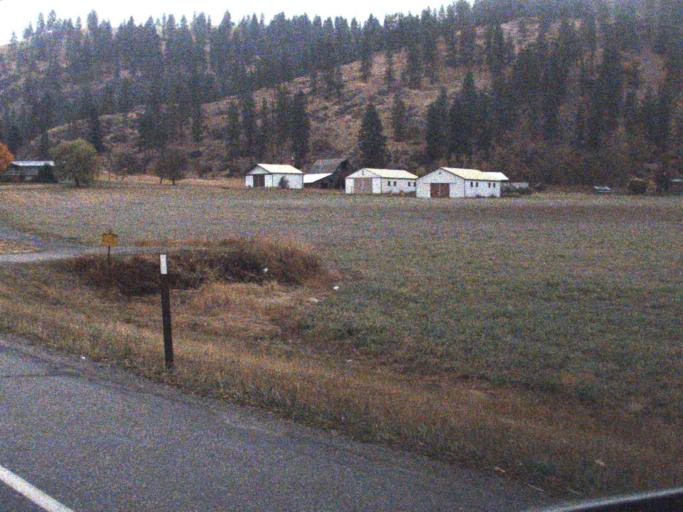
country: US
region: Washington
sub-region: Stevens County
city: Colville
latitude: 48.5839
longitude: -117.9662
